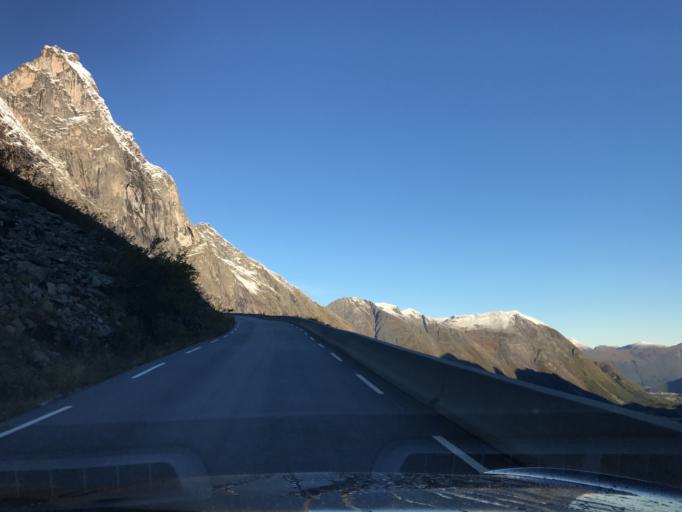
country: NO
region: More og Romsdal
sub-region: Rauma
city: Andalsnes
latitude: 62.4611
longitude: 7.6671
